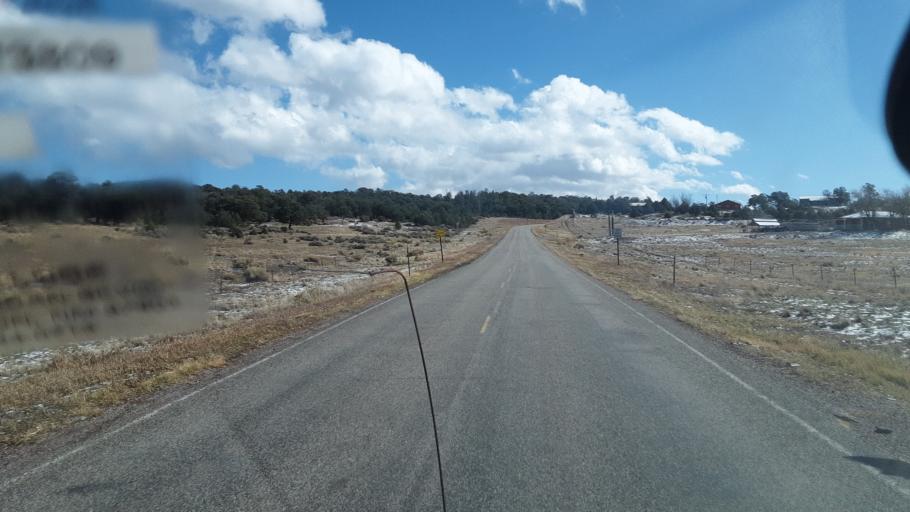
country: US
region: New Mexico
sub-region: Rio Arriba County
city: Santa Teresa
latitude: 36.2325
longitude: -106.8357
